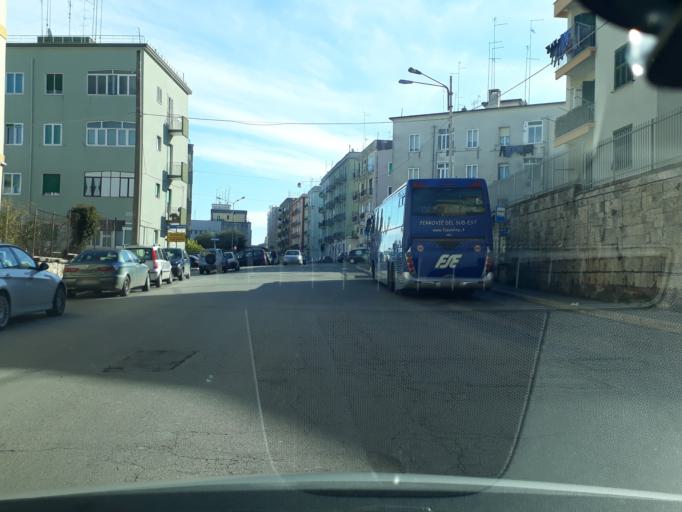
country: IT
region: Apulia
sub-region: Provincia di Taranto
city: Martina Franca
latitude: 40.7058
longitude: 17.3420
